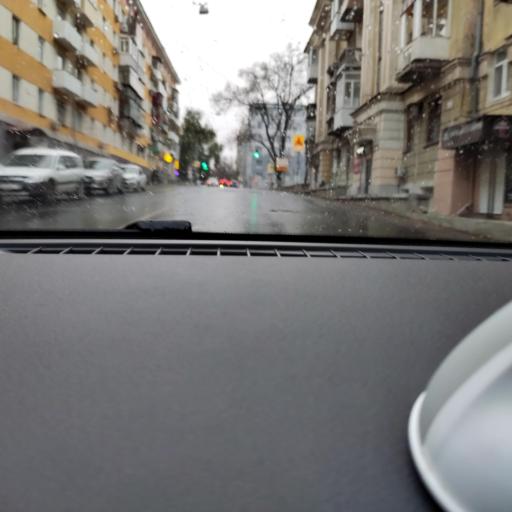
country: RU
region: Samara
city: Samara
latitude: 53.2073
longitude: 50.1260
